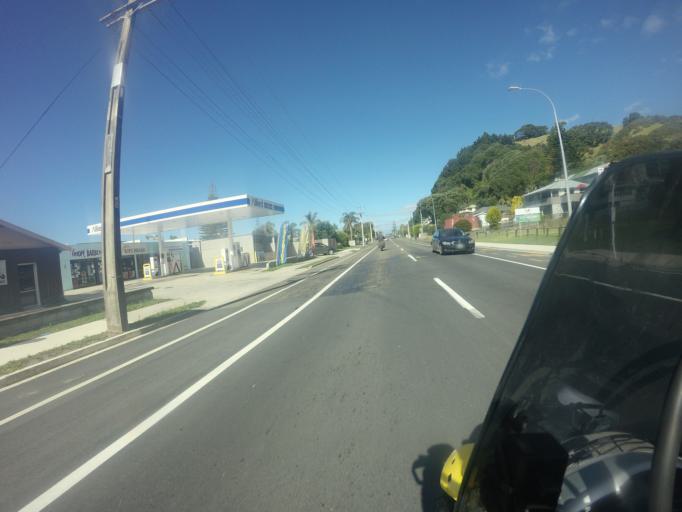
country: NZ
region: Bay of Plenty
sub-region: Whakatane District
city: Whakatane
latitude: -37.9654
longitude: 177.0391
